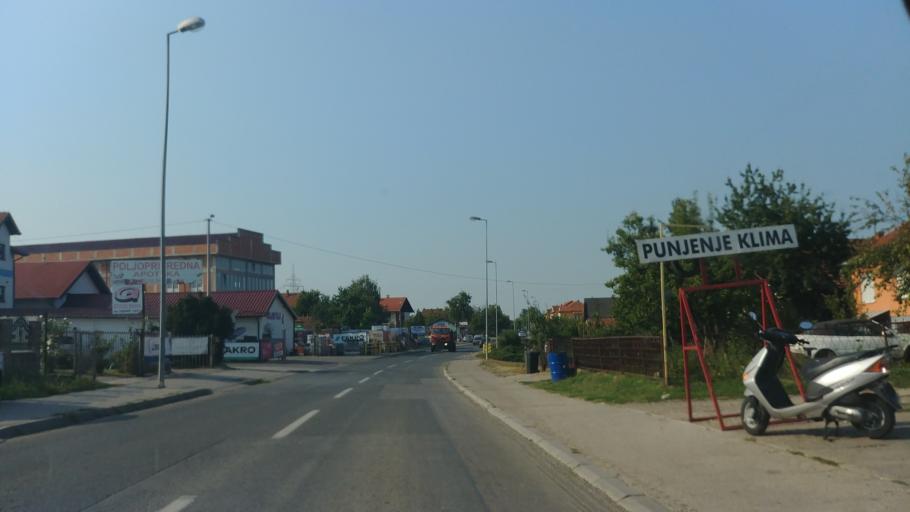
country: BA
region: Brcko
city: Brcko
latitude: 44.8530
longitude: 18.8147
